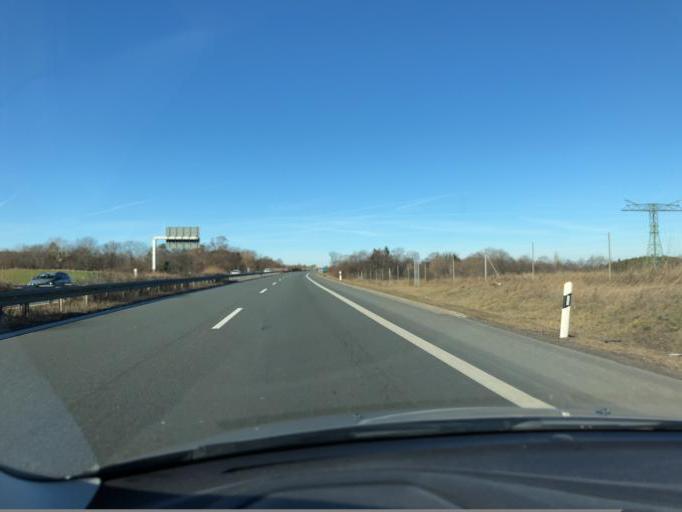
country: DE
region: Saxony-Anhalt
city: Blankenburg
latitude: 51.8130
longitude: 10.9396
